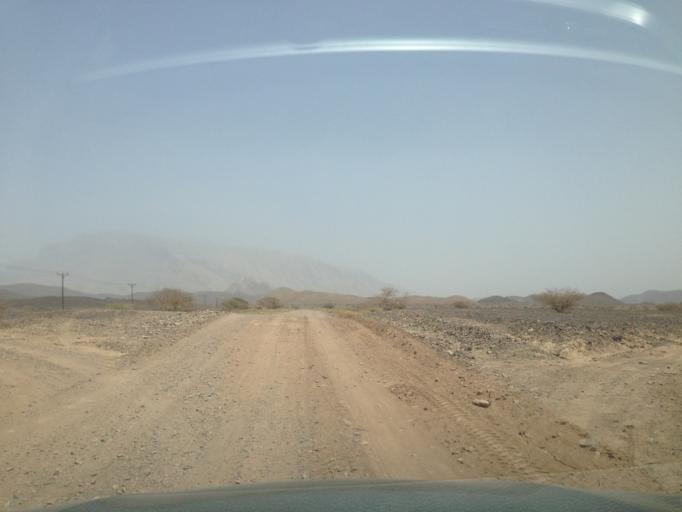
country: OM
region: Az Zahirah
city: `Ibri
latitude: 23.2145
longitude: 56.8340
